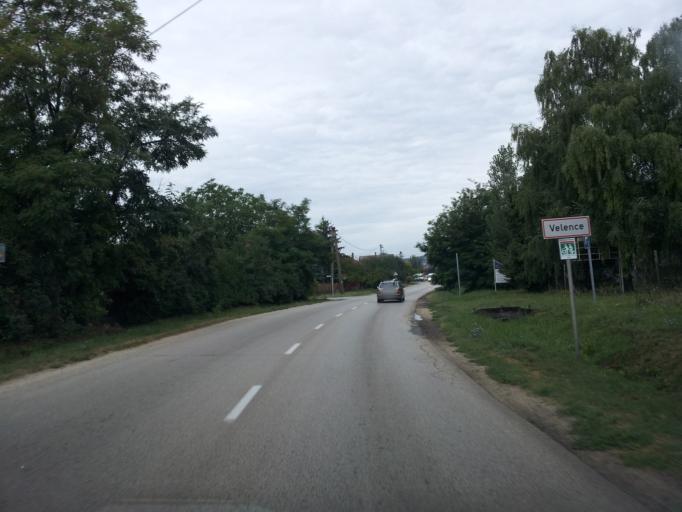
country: HU
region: Fejer
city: Velence
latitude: 47.2389
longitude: 18.6597
